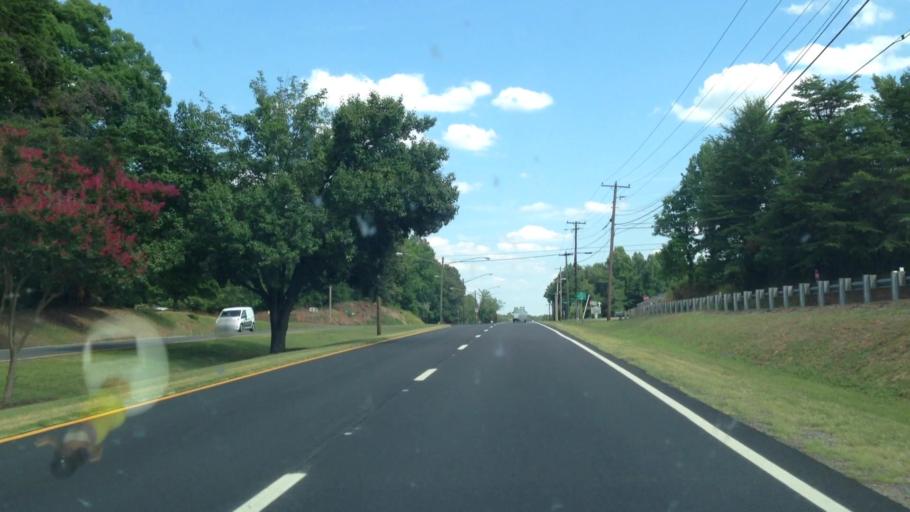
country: US
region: Virginia
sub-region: City of Danville
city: Danville
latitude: 36.5870
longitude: -79.4506
